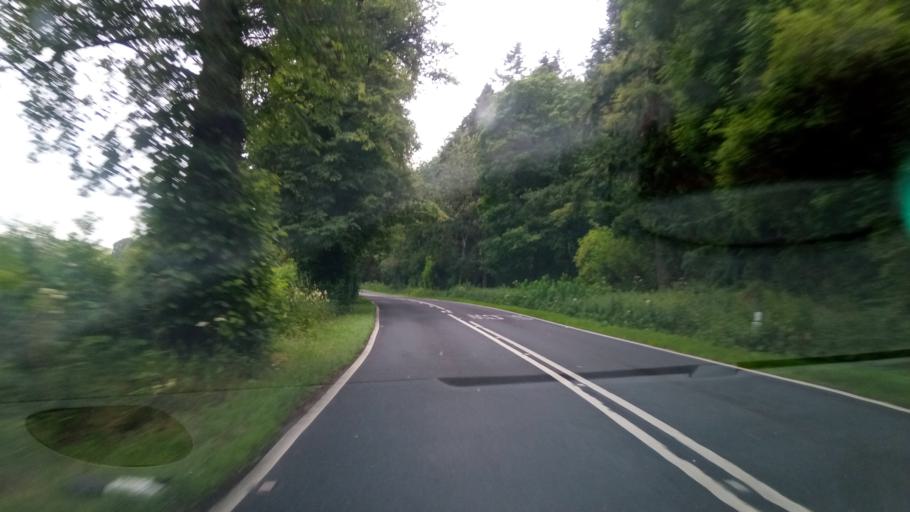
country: GB
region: Scotland
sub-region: The Scottish Borders
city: Hawick
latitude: 55.3949
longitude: -2.8490
